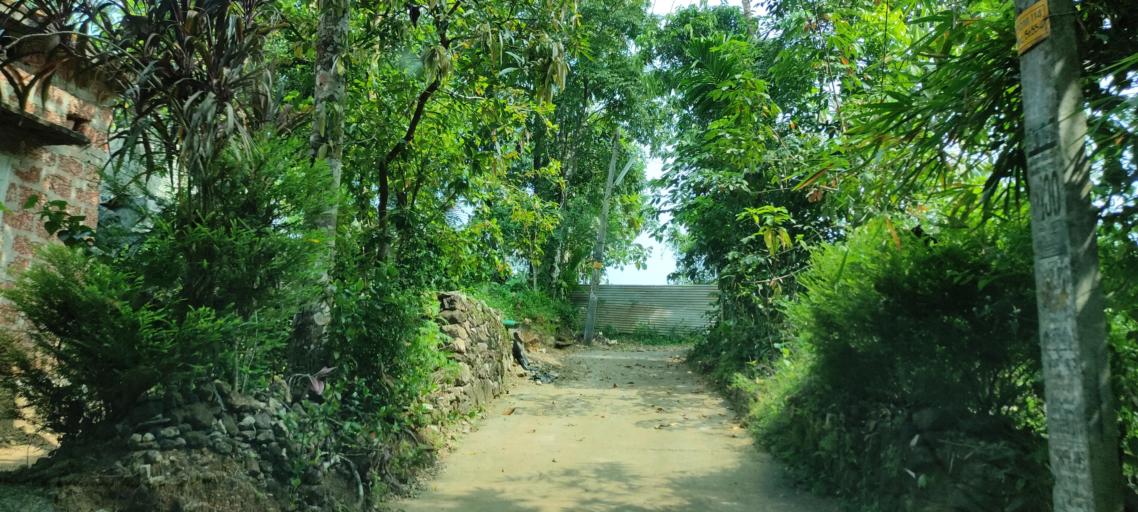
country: IN
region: Kerala
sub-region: Pattanamtitta
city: Adur
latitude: 9.2123
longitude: 76.6971
